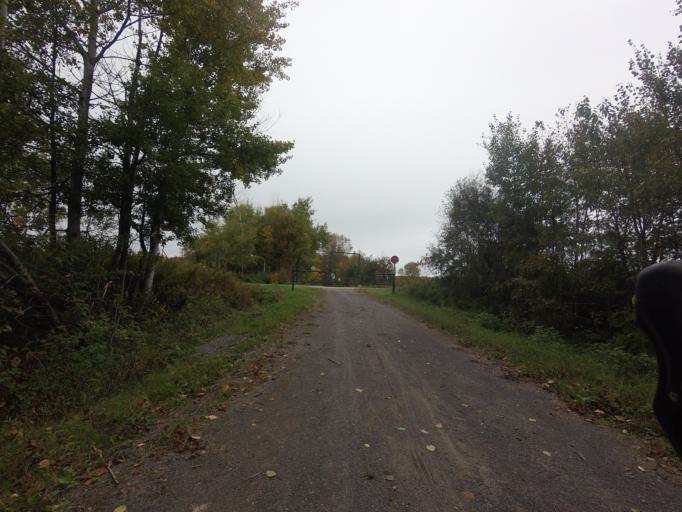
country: CA
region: Quebec
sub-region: Outaouais
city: Shawville
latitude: 45.6302
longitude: -76.5100
